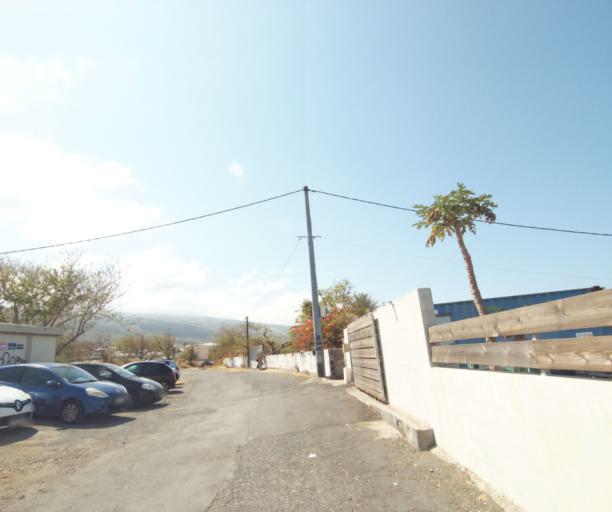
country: RE
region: Reunion
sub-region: Reunion
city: Trois-Bassins
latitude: -21.1033
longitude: 55.2470
